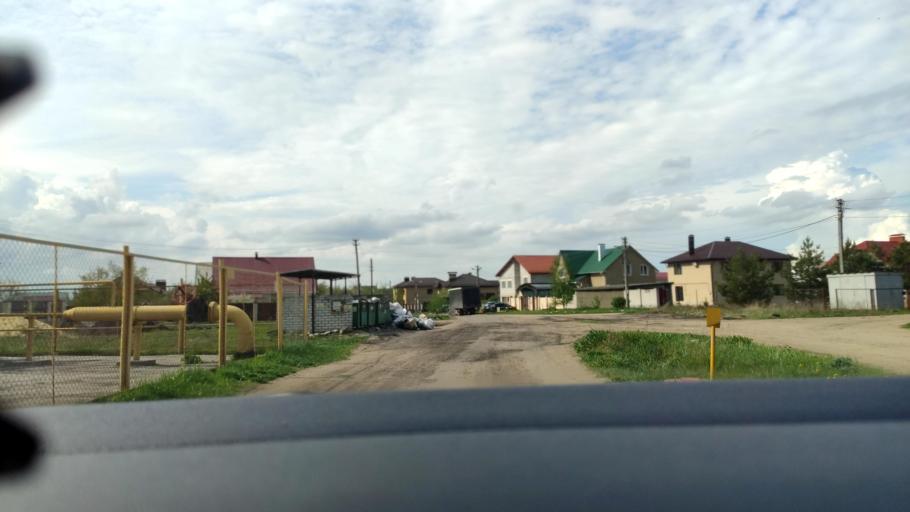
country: RU
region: Voronezj
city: Shilovo
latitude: 51.5653
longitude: 39.1127
